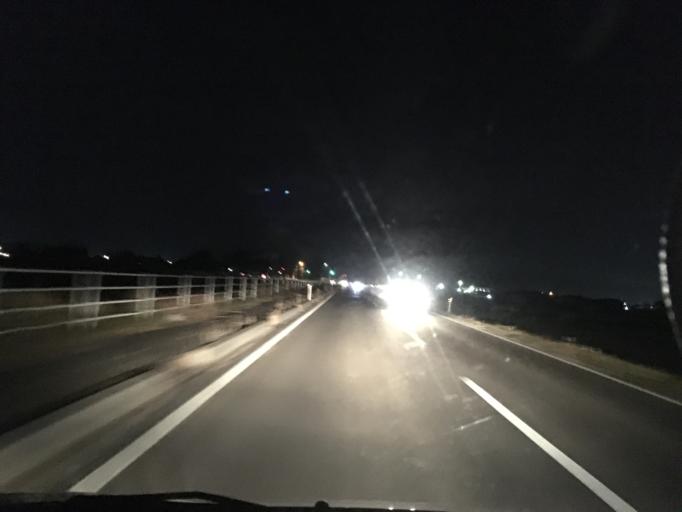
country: JP
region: Miyagi
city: Wakuya
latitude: 38.7127
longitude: 141.2173
